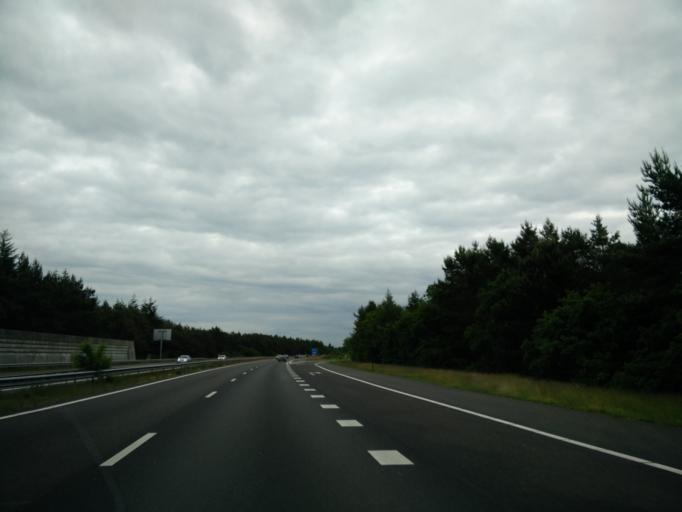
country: NL
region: Gelderland
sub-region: Gemeente Apeldoorn
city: Beekbergen
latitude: 52.1787
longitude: 5.9381
